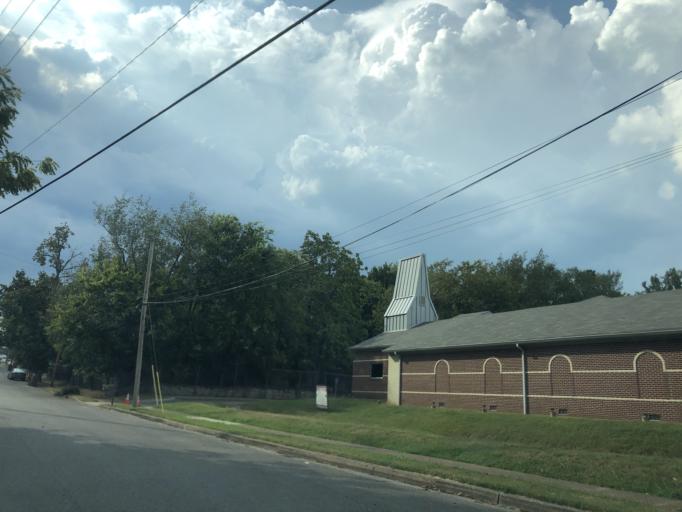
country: US
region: Tennessee
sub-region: Davidson County
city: Nashville
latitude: 36.1359
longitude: -86.7763
